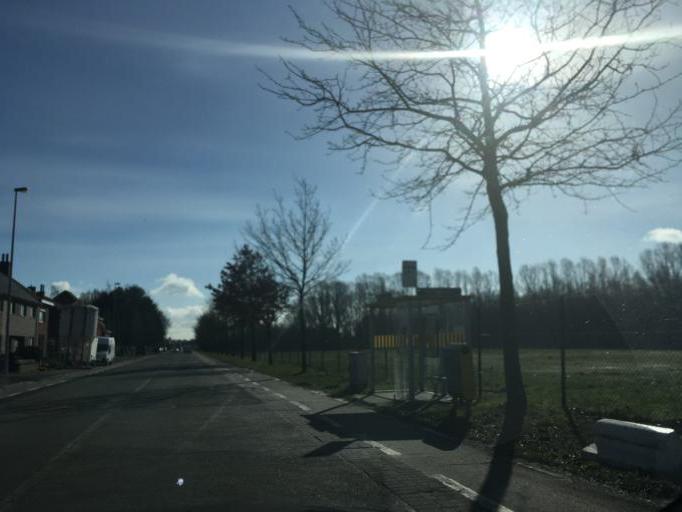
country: BE
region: Flanders
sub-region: Provincie West-Vlaanderen
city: Wevelgem
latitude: 50.8442
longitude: 3.1861
